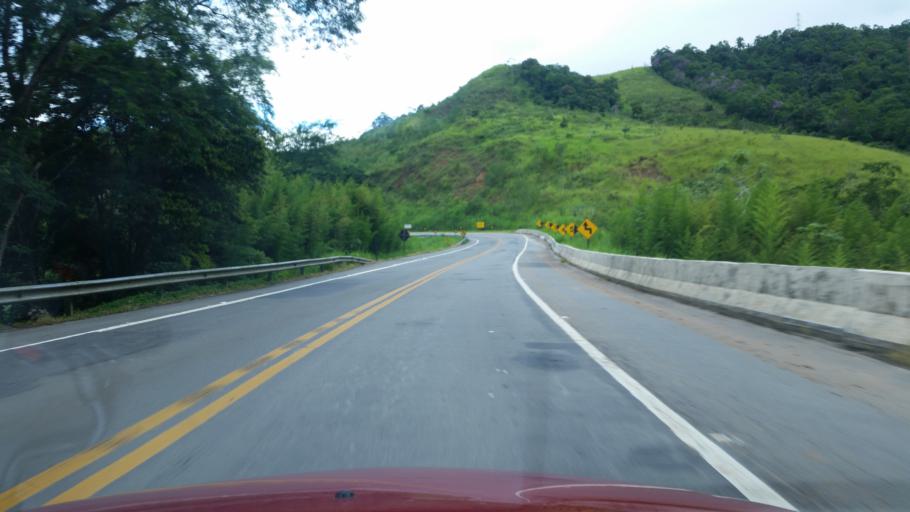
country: BR
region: Sao Paulo
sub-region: Miracatu
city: Miracatu
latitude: -24.2655
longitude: -47.2997
